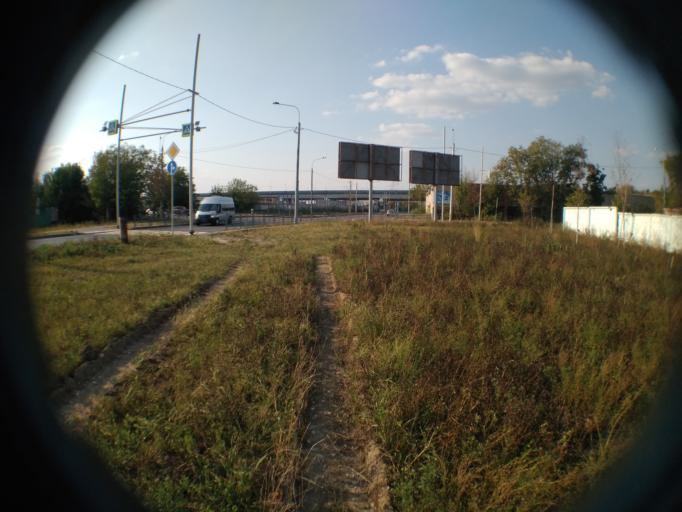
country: RU
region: Moskovskaya
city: Zhukovskiy
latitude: 55.5722
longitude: 38.1155
